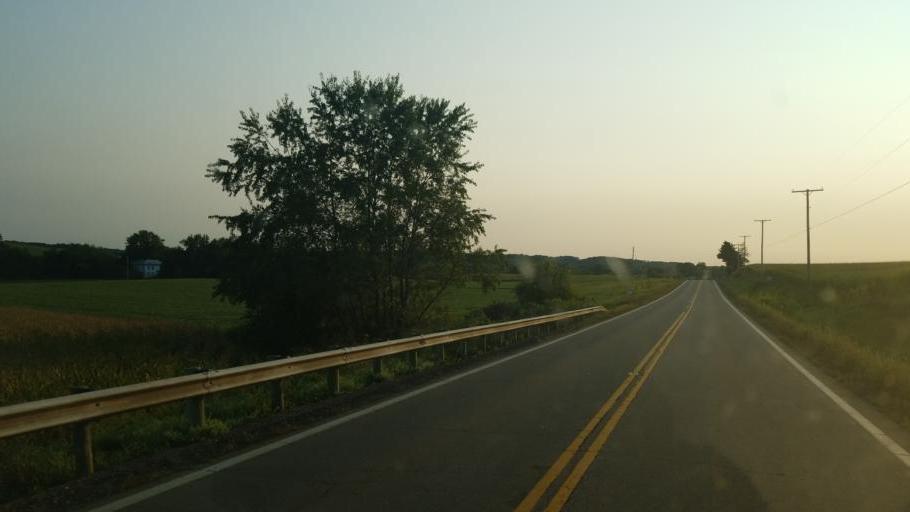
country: US
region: Ohio
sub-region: Ashland County
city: Loudonville
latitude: 40.6612
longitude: -82.1599
